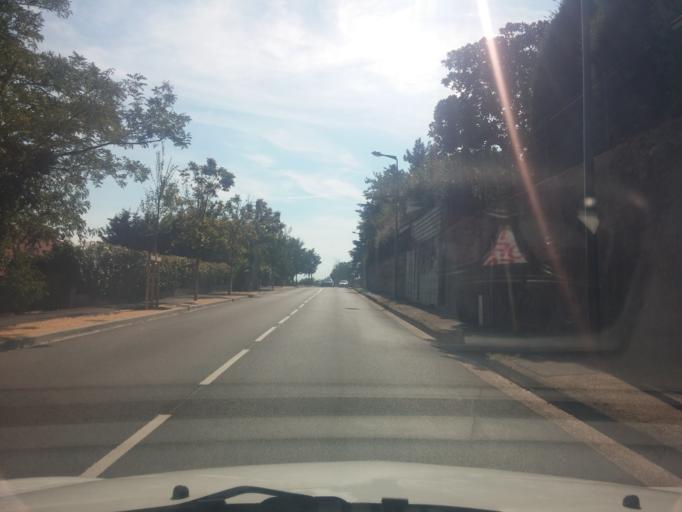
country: FR
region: Rhone-Alpes
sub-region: Departement du Rhone
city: Sainte-Foy-les-Lyon
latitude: 45.7302
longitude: 4.7976
